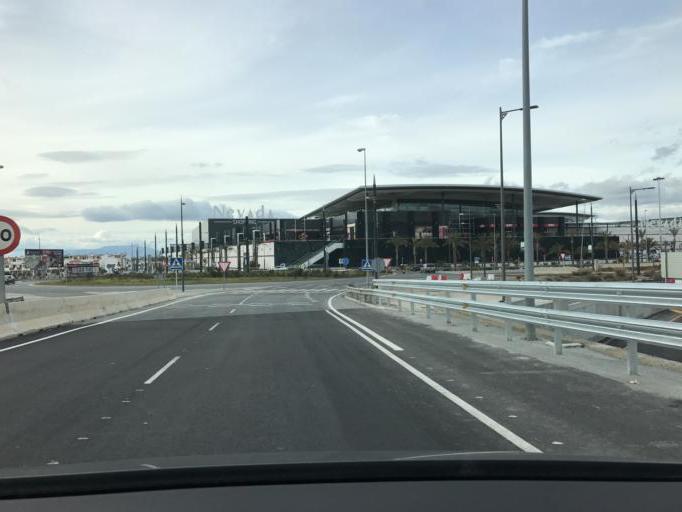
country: ES
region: Andalusia
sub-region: Provincia de Granada
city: Armilla
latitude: 37.1429
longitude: -3.6125
